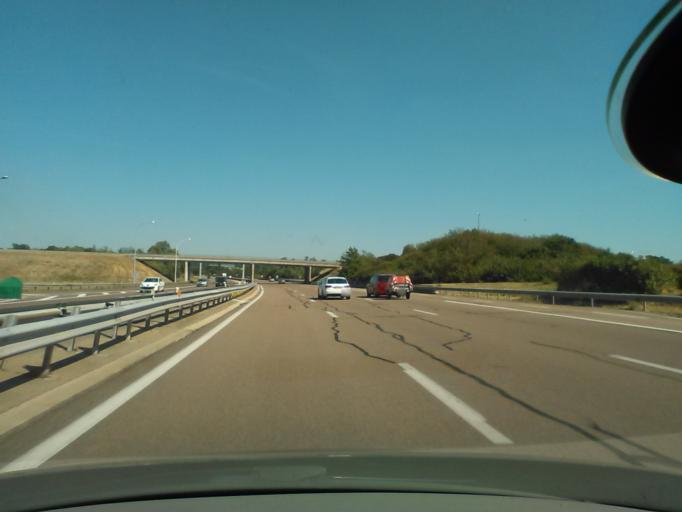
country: FR
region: Bourgogne
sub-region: Departement de l'Yonne
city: Gurgy
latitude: 47.8557
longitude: 3.5463
